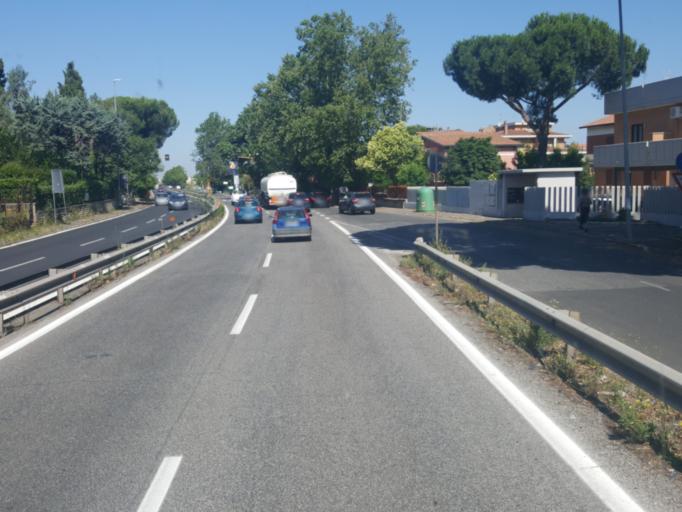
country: IT
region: Latium
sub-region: Citta metropolitana di Roma Capitale
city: Ciampino
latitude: 41.8314
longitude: 12.6184
